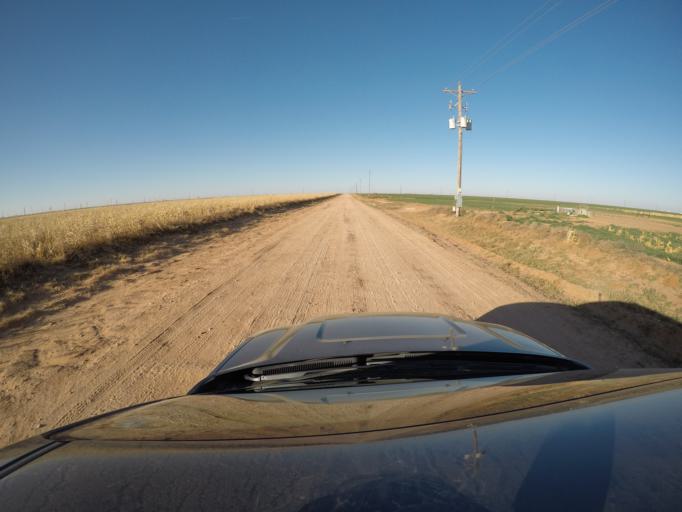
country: US
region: New Mexico
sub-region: Curry County
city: Texico
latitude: 34.3528
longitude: -103.1083
